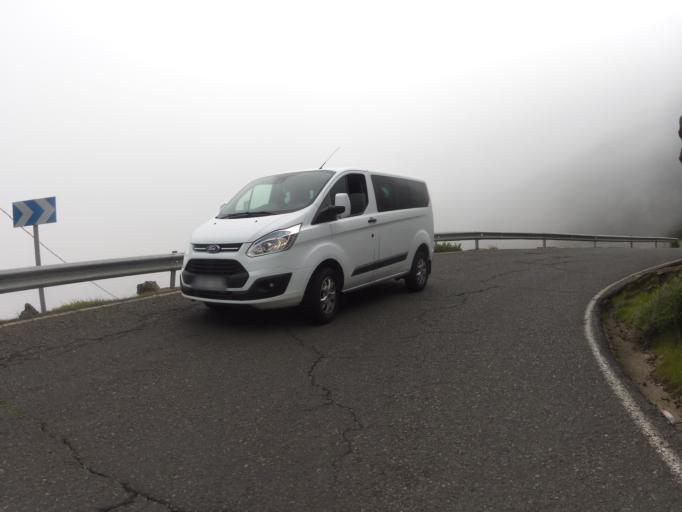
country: ES
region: Canary Islands
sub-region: Provincia de Las Palmas
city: Tejeda
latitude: 27.9857
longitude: -15.5761
